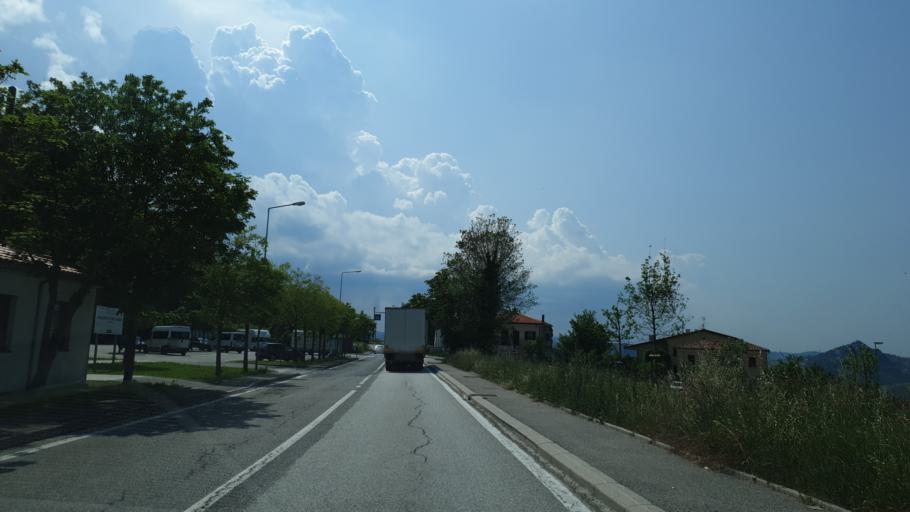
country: SM
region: Acquaviva
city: Acquaviva
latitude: 43.9470
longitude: 12.4253
